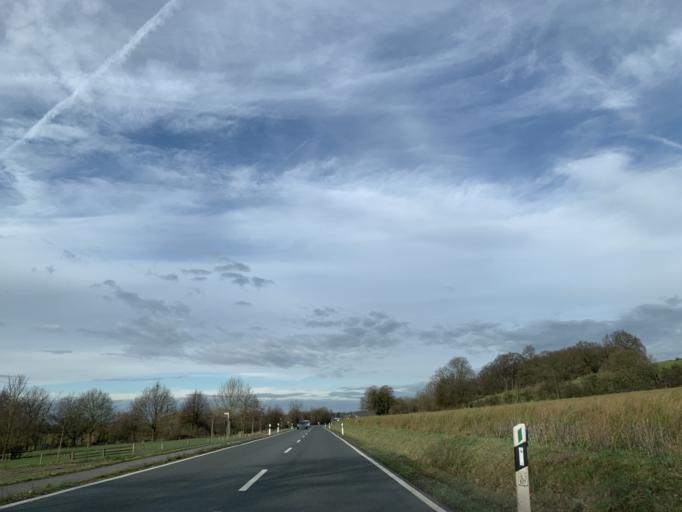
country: DE
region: North Rhine-Westphalia
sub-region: Regierungsbezirk Munster
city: Billerbeck
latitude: 51.9644
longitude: 7.3091
